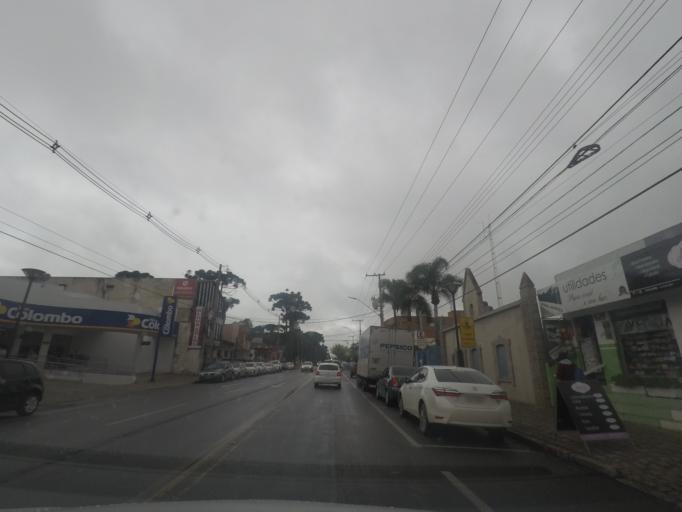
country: BR
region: Parana
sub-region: Quatro Barras
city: Quatro Barras
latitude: -25.3689
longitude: -49.0746
